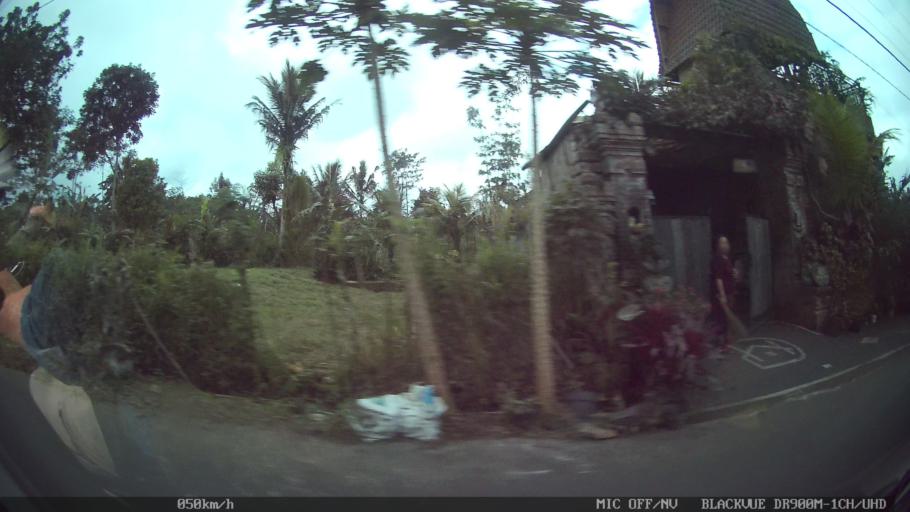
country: ID
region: Bali
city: Banjar Geriana Kangin
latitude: -8.3889
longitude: 115.4445
